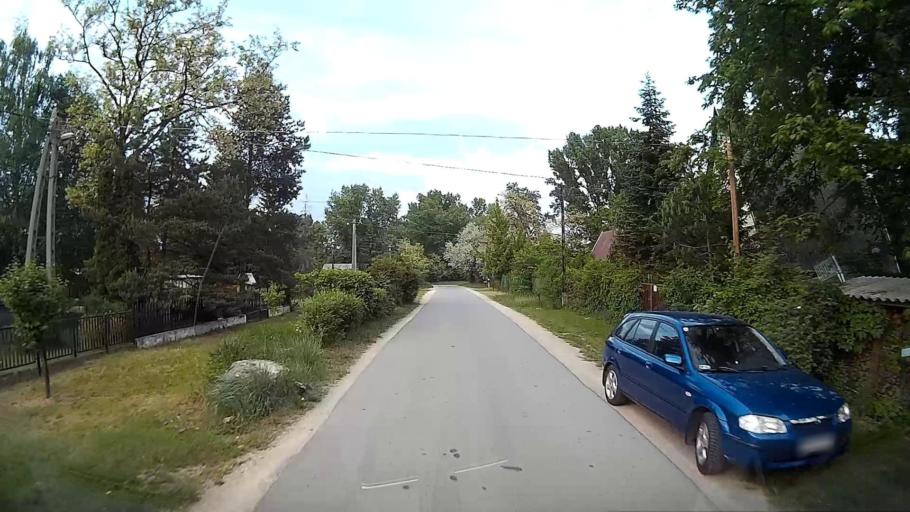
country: HU
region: Pest
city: God
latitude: 47.6697
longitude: 19.1109
